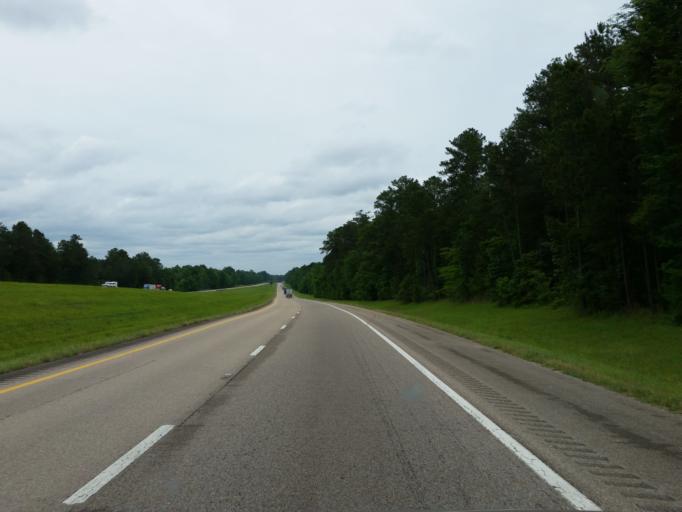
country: US
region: Mississippi
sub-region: Clarke County
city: Stonewall
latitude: 32.0201
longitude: -88.9230
